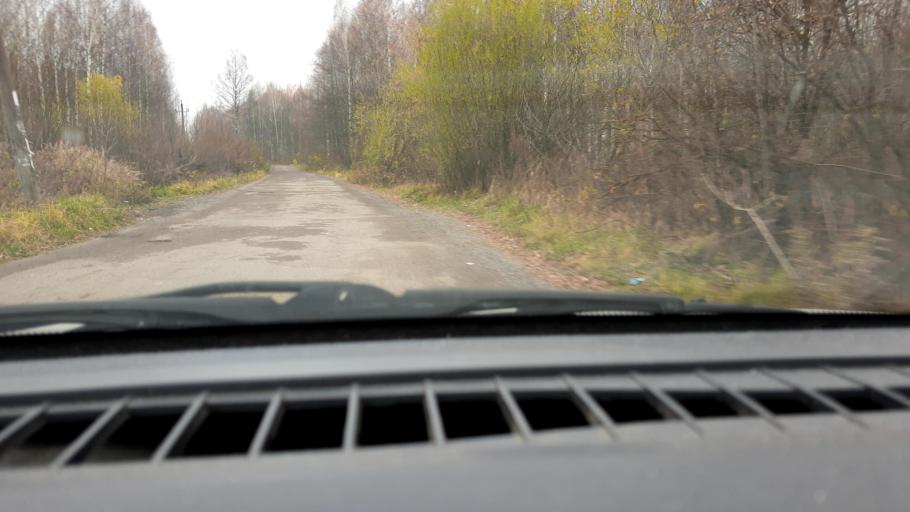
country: RU
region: Nizjnij Novgorod
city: Gorbatovka
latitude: 56.3063
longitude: 43.7250
